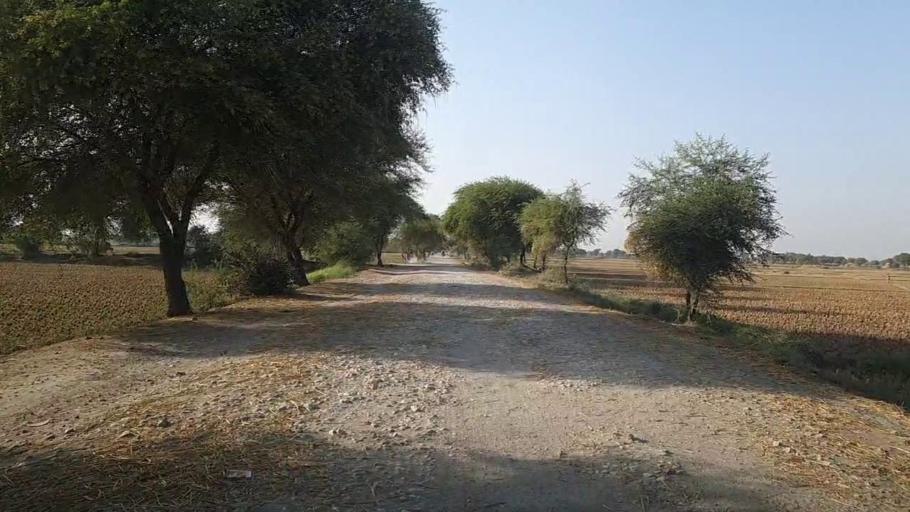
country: PK
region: Sindh
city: Kashmor
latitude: 28.4029
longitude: 69.4180
